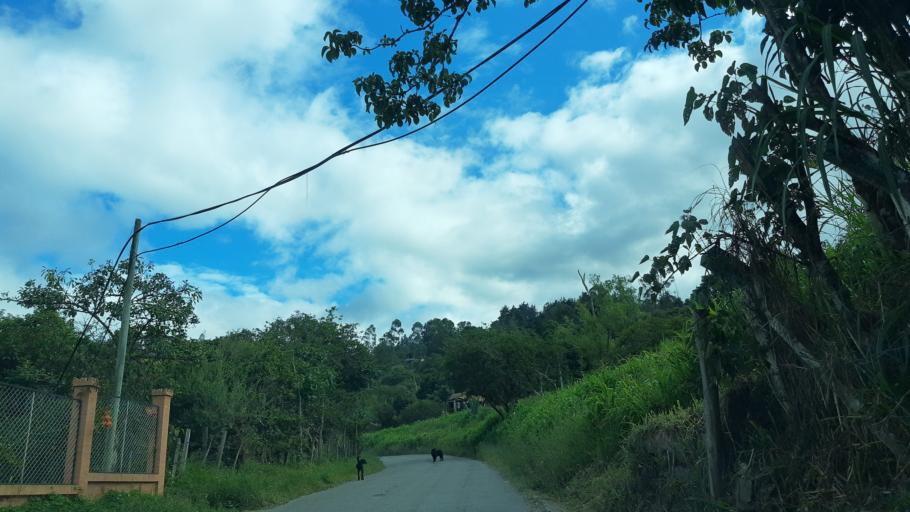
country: CO
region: Cundinamarca
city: Tenza
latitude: 5.0592
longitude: -73.4209
